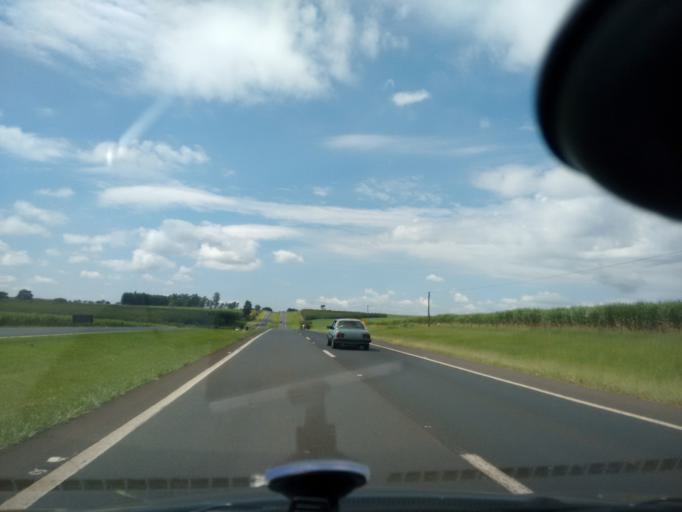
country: BR
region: Sao Paulo
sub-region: Ibate
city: Ibate
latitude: -21.9146
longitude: -48.0429
